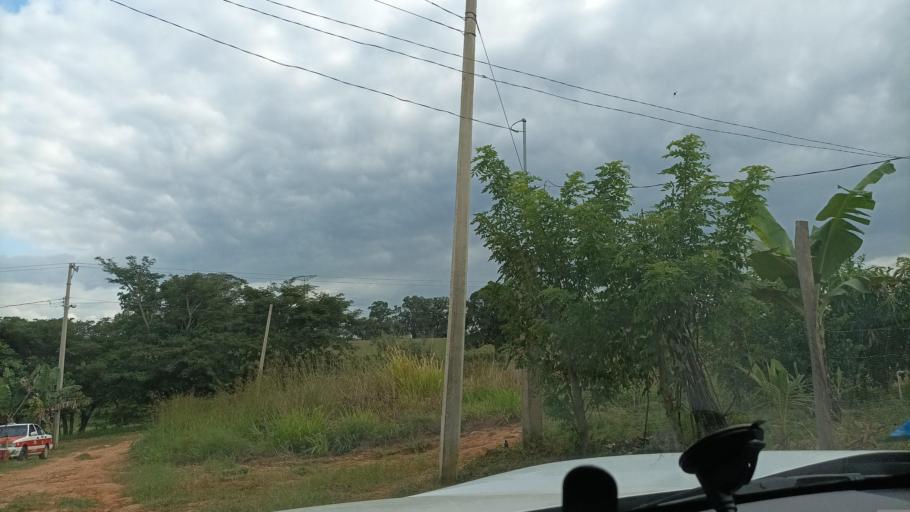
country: MX
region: Veracruz
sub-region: Soconusco
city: Colonia Lealtad
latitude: 17.9591
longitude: -94.8949
